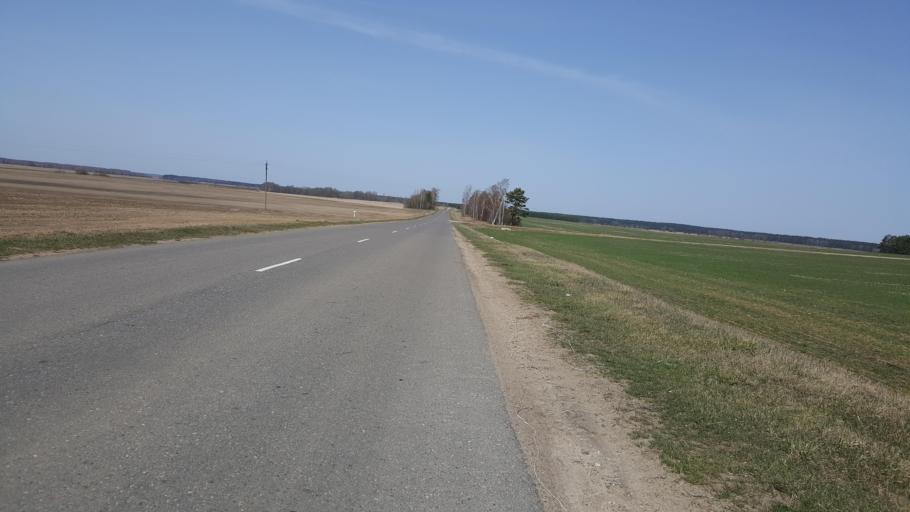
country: BY
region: Brest
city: Kamyanyuki
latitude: 52.4785
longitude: 23.7026
